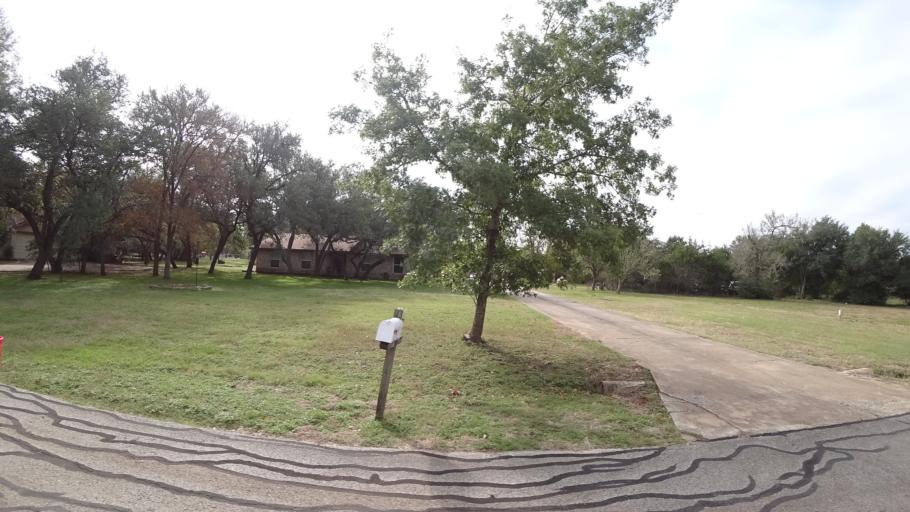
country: US
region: Texas
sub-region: Travis County
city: Shady Hollow
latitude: 30.1389
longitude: -97.8928
